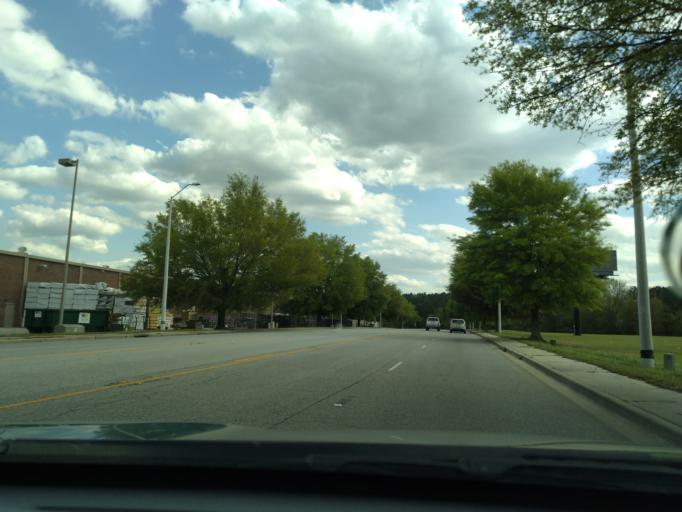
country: US
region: South Carolina
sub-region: Florence County
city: Florence
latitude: 34.1606
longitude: -79.7599
